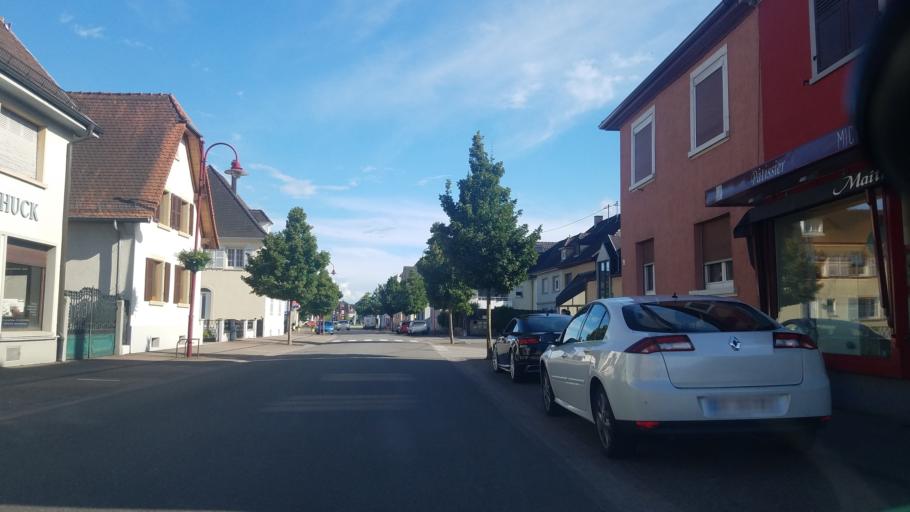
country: FR
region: Alsace
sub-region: Departement du Bas-Rhin
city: Drusenheim
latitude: 48.7609
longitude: 7.9517
